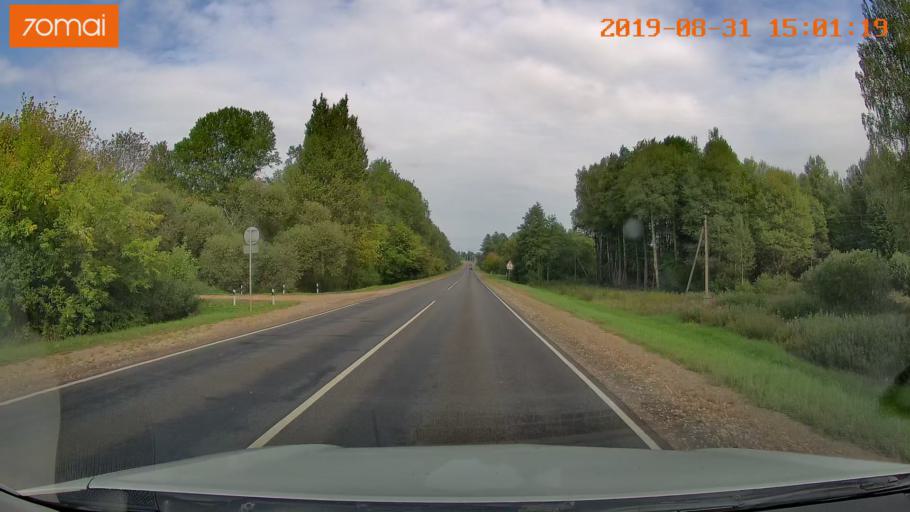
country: RU
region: Kaluga
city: Spas-Demensk
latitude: 54.3384
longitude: 34.0534
